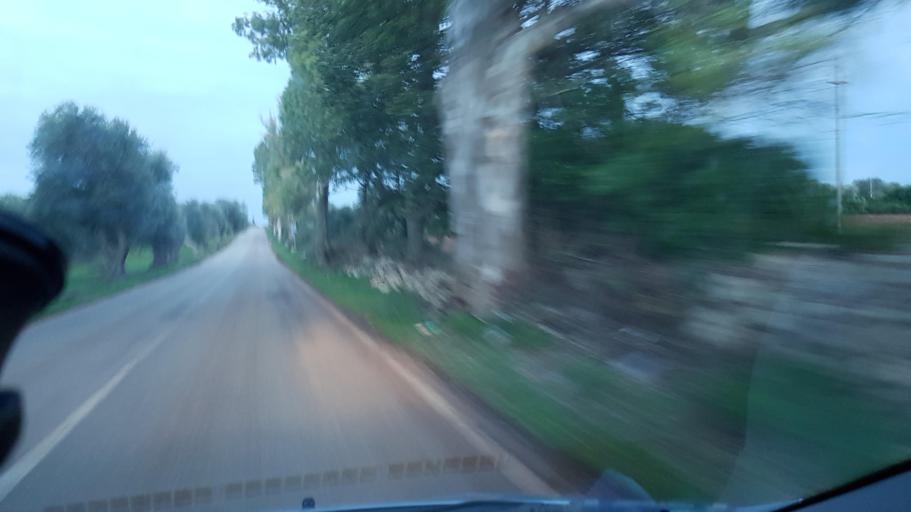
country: IT
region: Apulia
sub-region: Provincia di Brindisi
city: San Michele Salentino
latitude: 40.6431
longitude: 17.6004
